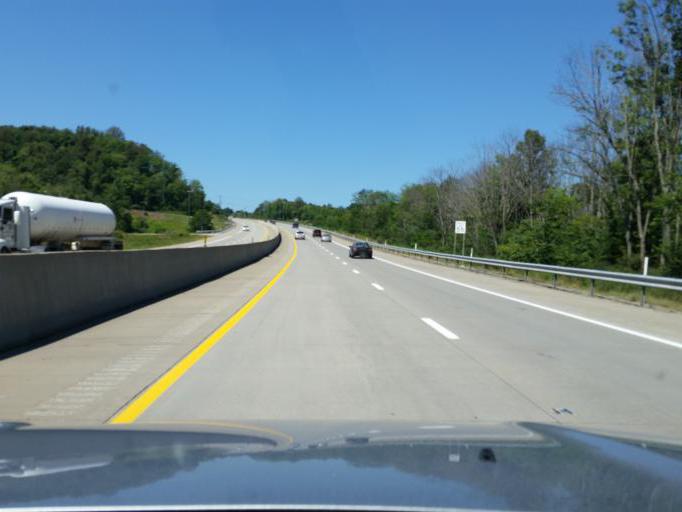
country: US
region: Pennsylvania
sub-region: Indiana County
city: Blairsville
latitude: 40.4218
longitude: -79.3549
